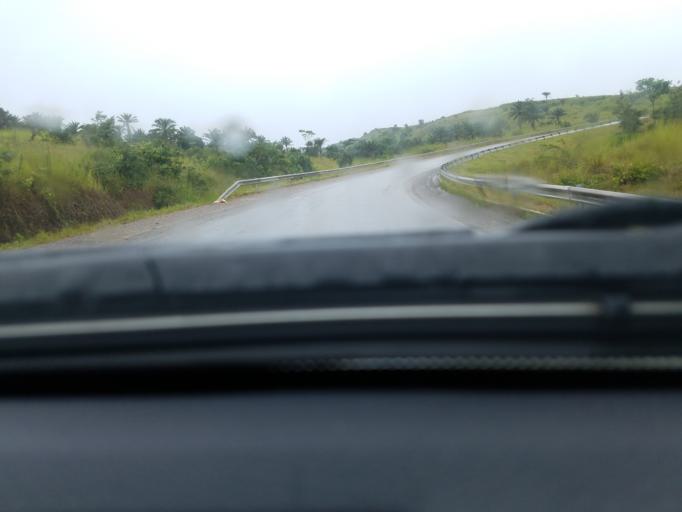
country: TZ
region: Kigoma
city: Mwandiga
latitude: -4.6698
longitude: 29.7242
